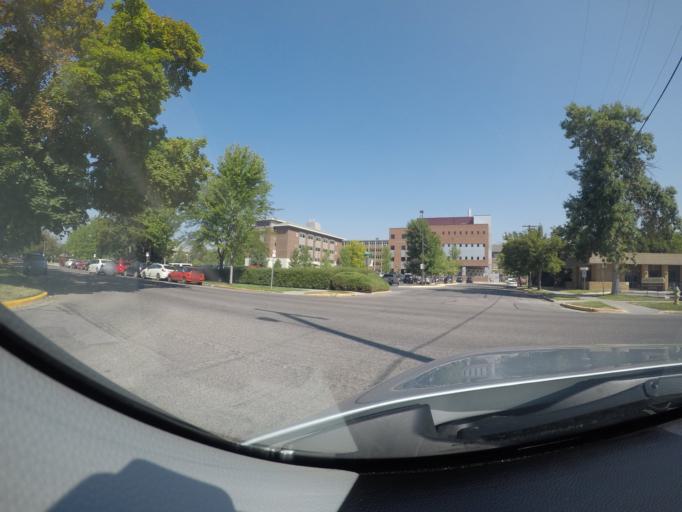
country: US
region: Montana
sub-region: Missoula County
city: Missoula
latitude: 46.8571
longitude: -113.9854
